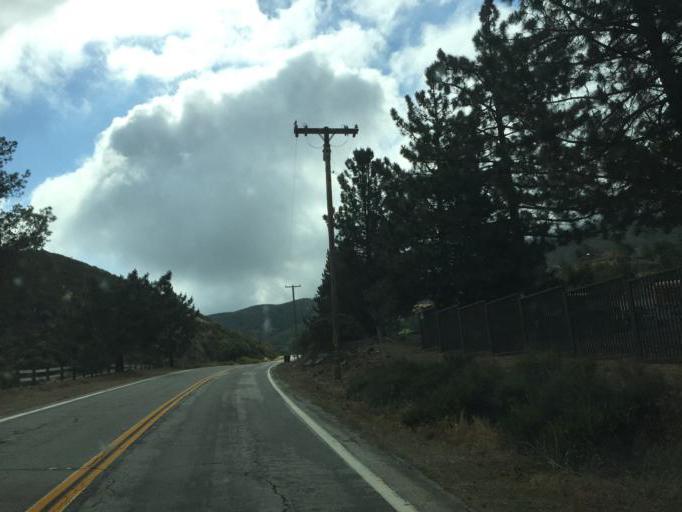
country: US
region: California
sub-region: Los Angeles County
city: Leona Valley
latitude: 34.5848
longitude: -118.3138
